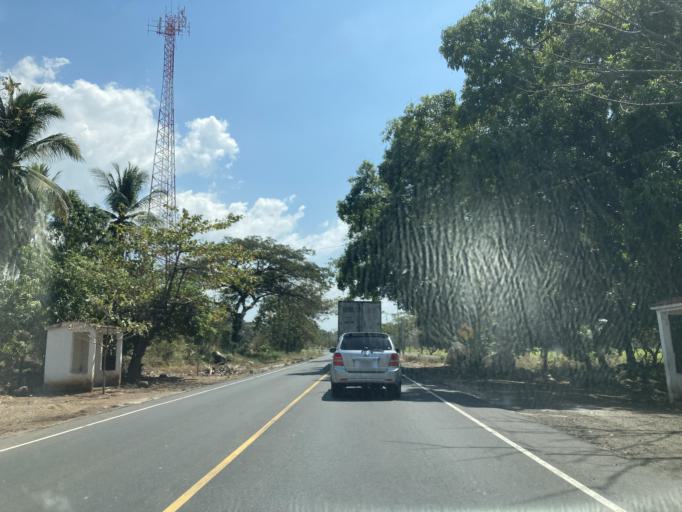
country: GT
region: Santa Rosa
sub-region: Municipio de Taxisco
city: Taxisco
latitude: 14.0919
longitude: -90.5667
